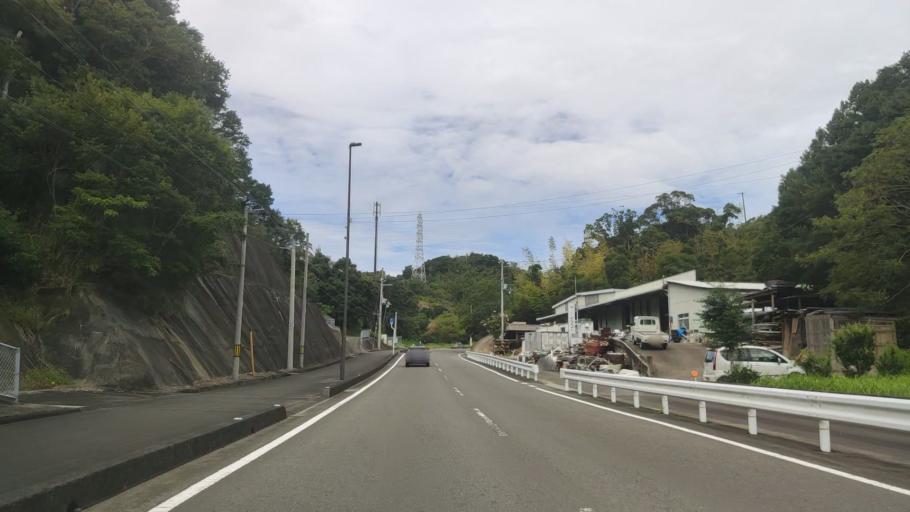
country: JP
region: Wakayama
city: Tanabe
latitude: 33.6834
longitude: 135.3882
